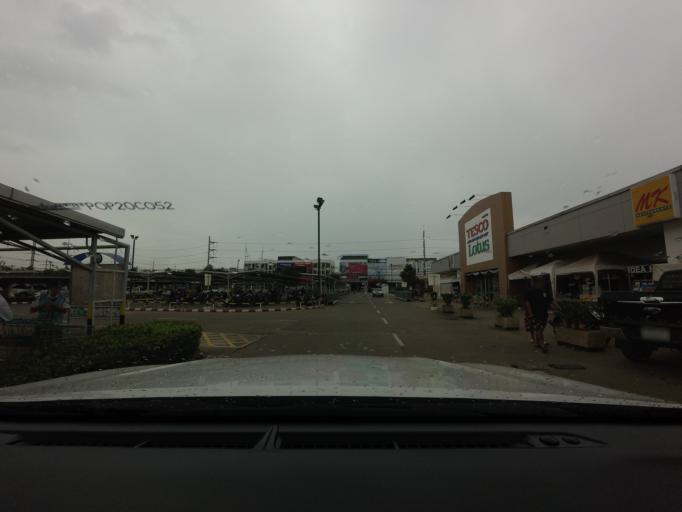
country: TH
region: Prachin Buri
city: Si Maha Phot
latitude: 13.8954
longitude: 101.5800
